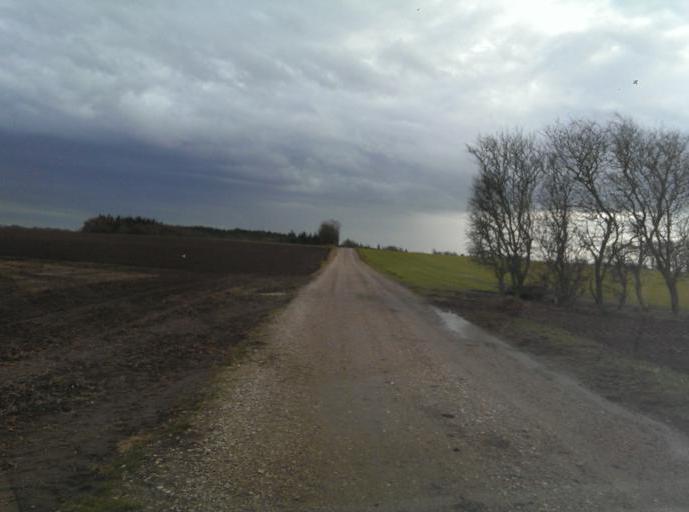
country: DK
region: South Denmark
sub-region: Esbjerg Kommune
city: Tjaereborg
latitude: 55.4849
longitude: 8.5991
